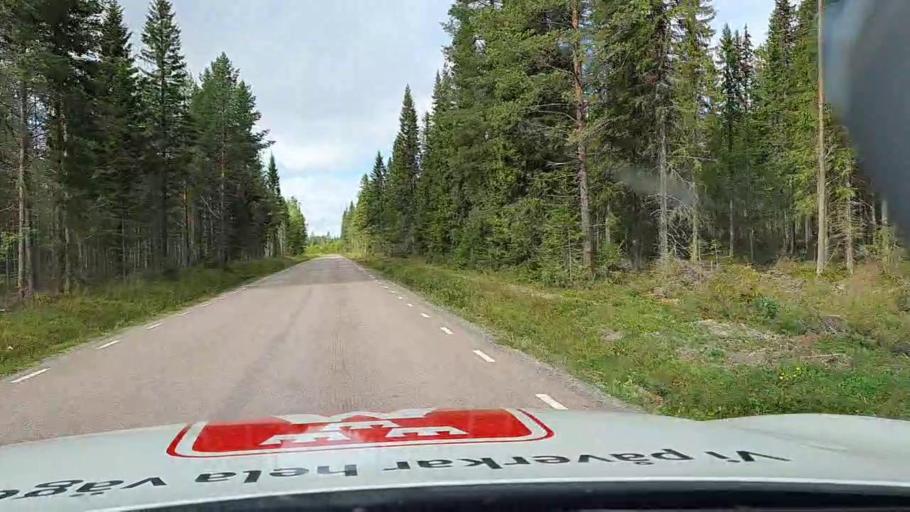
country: SE
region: Jaemtland
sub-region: Stroemsunds Kommun
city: Stroemsund
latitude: 63.8612
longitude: 15.3862
